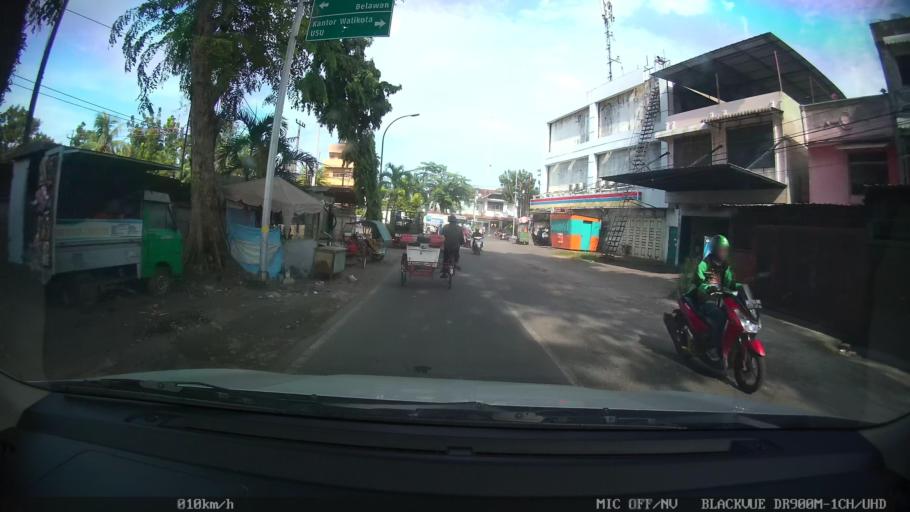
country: ID
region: North Sumatra
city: Medan
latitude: 3.6200
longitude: 98.6703
